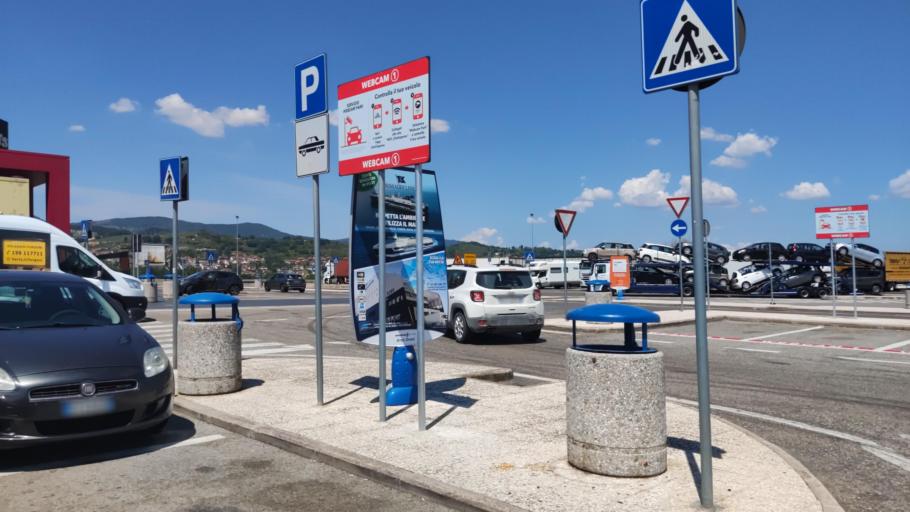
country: IT
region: Tuscany
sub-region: Province of Florence
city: Incisa in Val d'Arno
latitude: 43.6508
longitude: 11.4643
